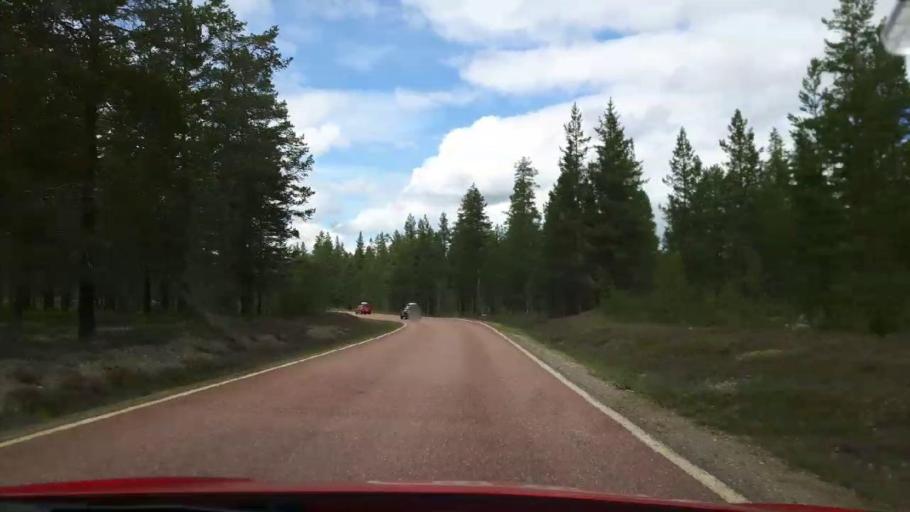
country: NO
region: Hedmark
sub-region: Trysil
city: Innbygda
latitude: 61.8498
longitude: 12.9539
